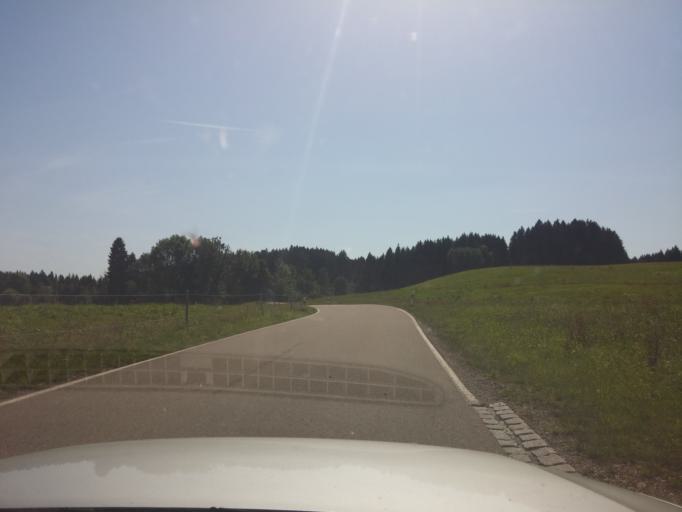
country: DE
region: Bavaria
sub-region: Swabia
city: Lautrach
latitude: 47.8773
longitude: 10.1065
